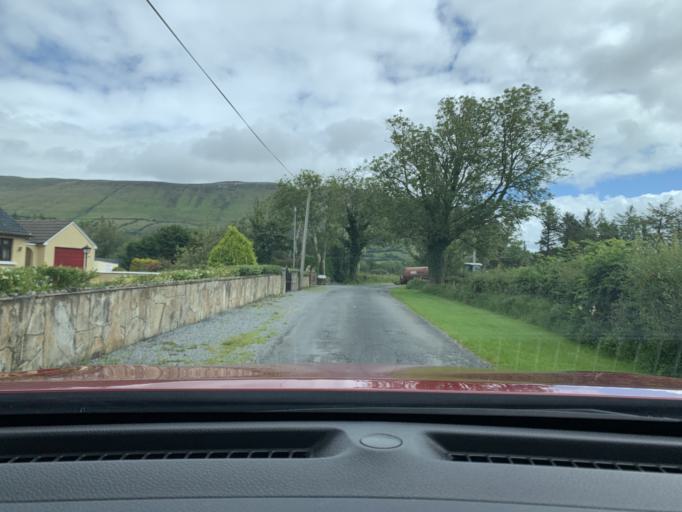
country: IE
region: Connaught
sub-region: Sligo
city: Sligo
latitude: 54.3357
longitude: -8.4931
